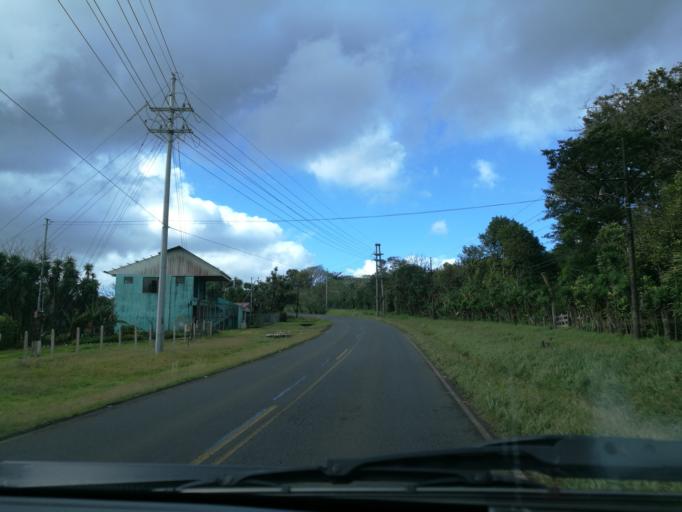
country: CR
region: Alajuela
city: Bijagua
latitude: 10.6875
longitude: -85.0863
